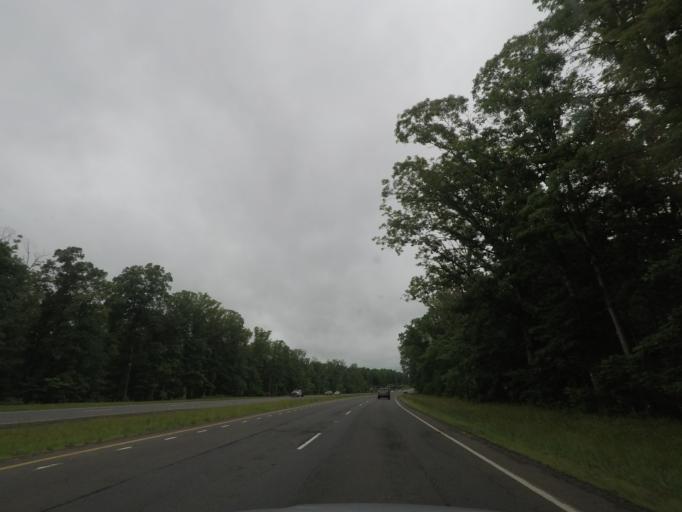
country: US
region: Virginia
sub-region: Prince William County
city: Haymarket
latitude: 38.8046
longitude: -77.6598
